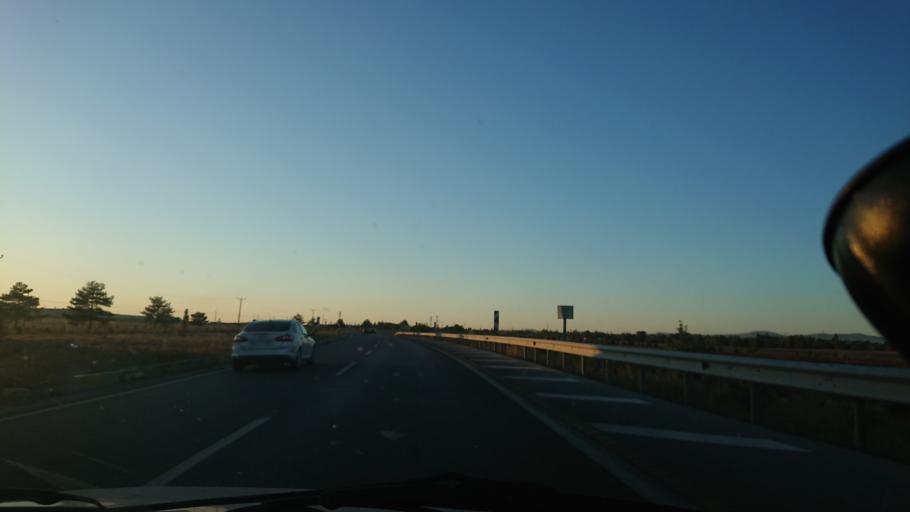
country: TR
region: Eskisehir
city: Mahmudiye
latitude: 39.5555
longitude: 30.9221
